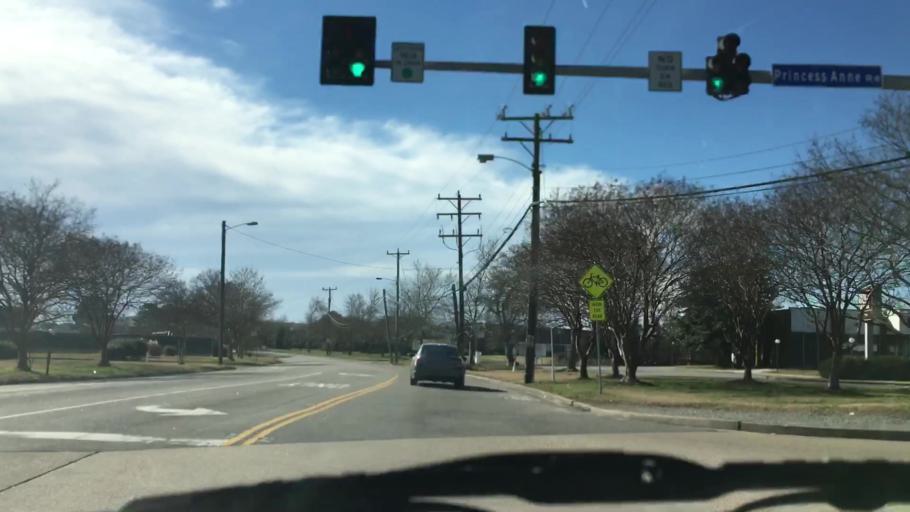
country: US
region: Virginia
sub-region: City of Norfolk
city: Norfolk
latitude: 36.8667
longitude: -76.2349
